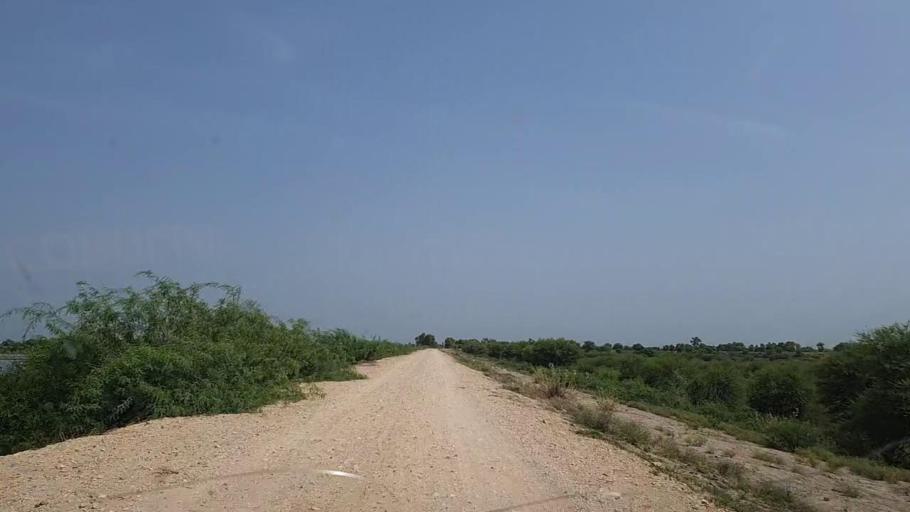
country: PK
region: Sindh
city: Ghotki
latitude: 28.0920
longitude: 69.4081
